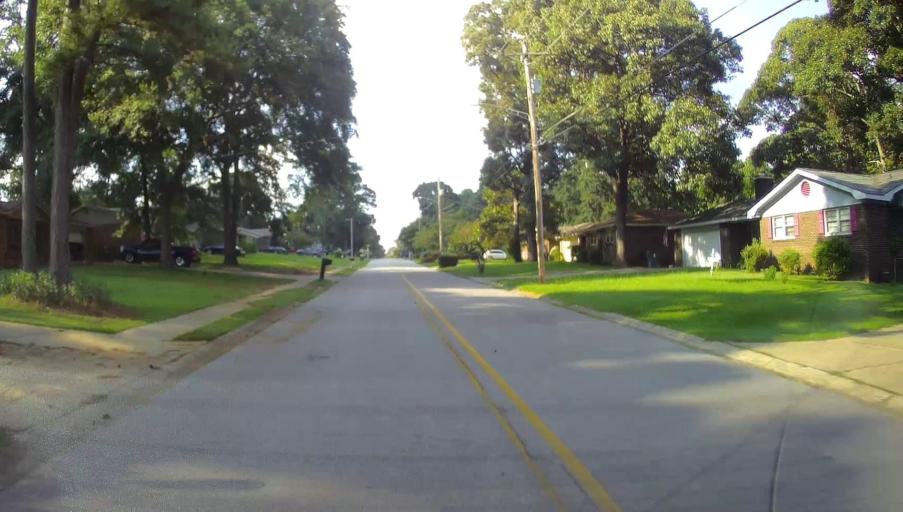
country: US
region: Georgia
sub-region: Houston County
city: Warner Robins
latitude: 32.5867
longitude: -83.6442
